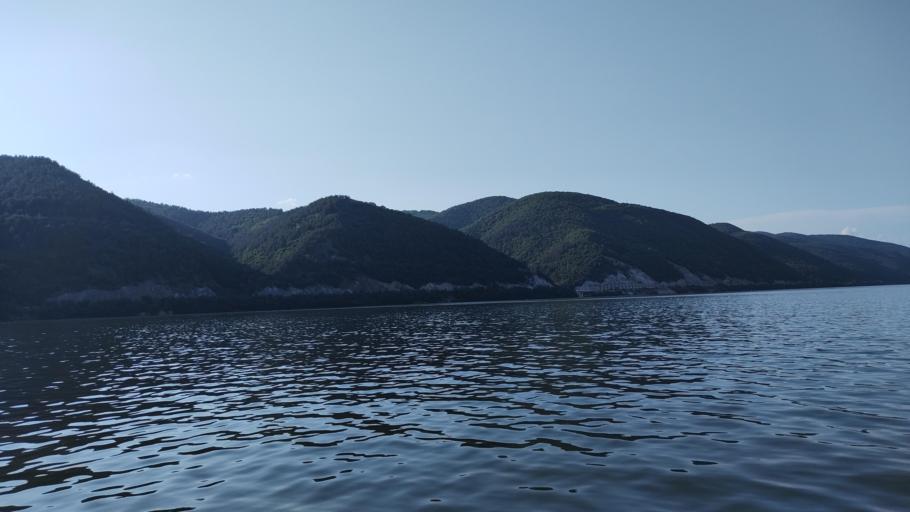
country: RO
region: Mehedinti
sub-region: Comuna Dubova
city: Dubova
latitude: 44.5332
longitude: 22.2141
